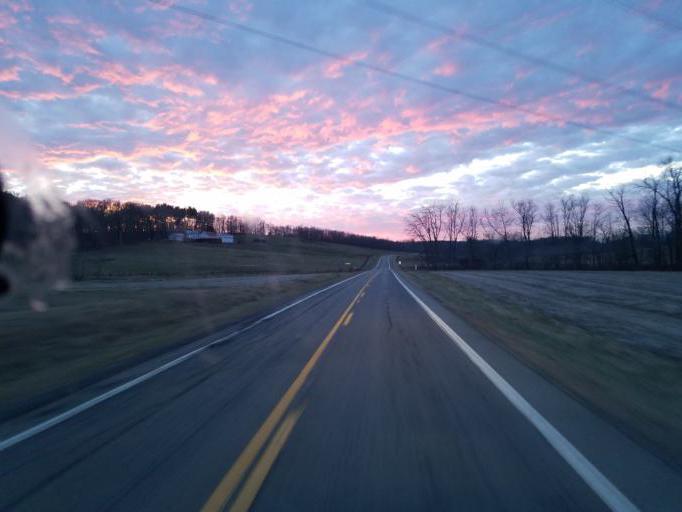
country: US
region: Ohio
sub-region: Knox County
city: Oak Hill
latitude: 40.2895
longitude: -82.2212
